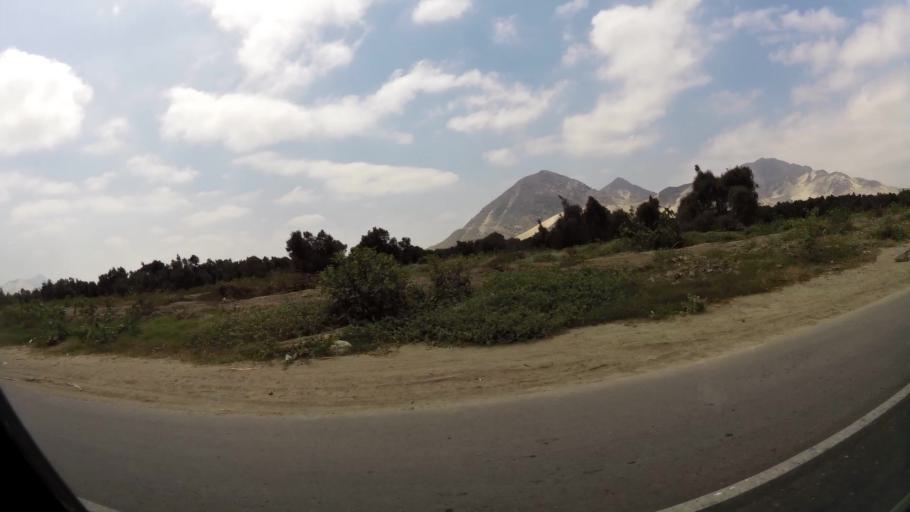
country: PE
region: La Libertad
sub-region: Ascope
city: Paijan
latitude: -7.6801
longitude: -79.3239
